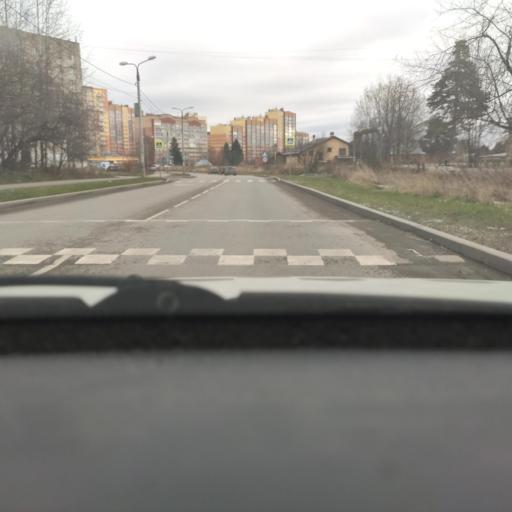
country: RU
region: Perm
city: Perm
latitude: 58.0854
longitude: 56.3989
